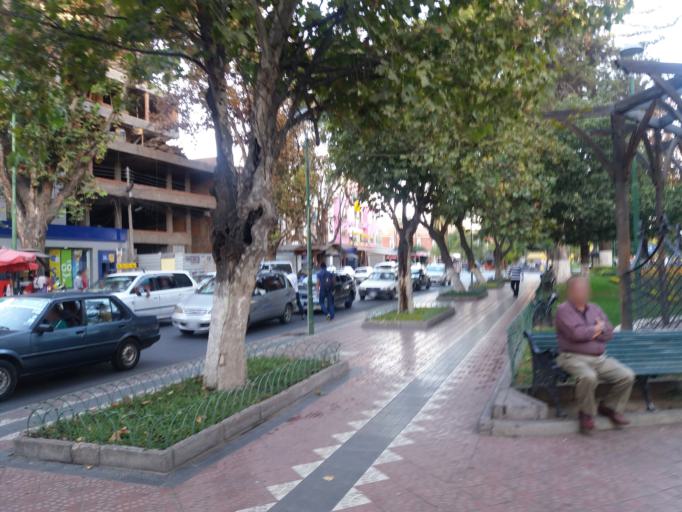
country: BO
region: Cochabamba
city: Cochabamba
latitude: -17.3869
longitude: -66.1563
